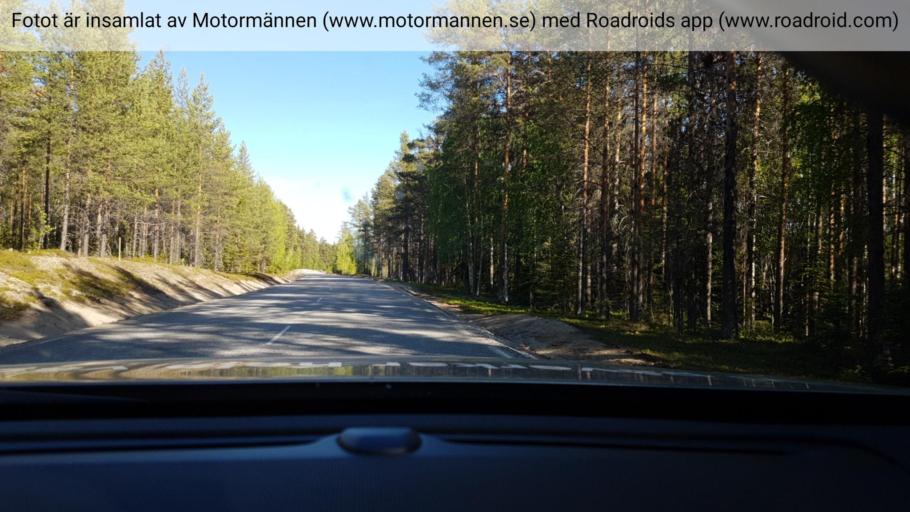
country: SE
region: Vaesterbotten
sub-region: Norsjo Kommun
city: Norsjoe
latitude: 64.6967
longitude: 19.1790
